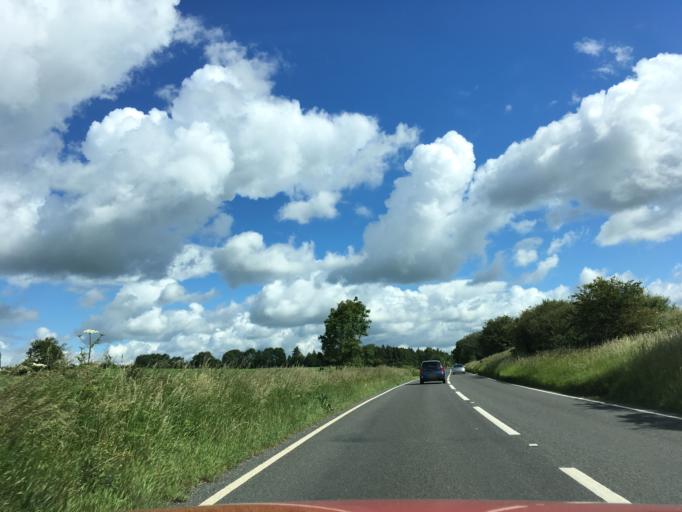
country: GB
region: England
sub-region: Oxfordshire
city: Burford
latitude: 51.7943
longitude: -1.6440
